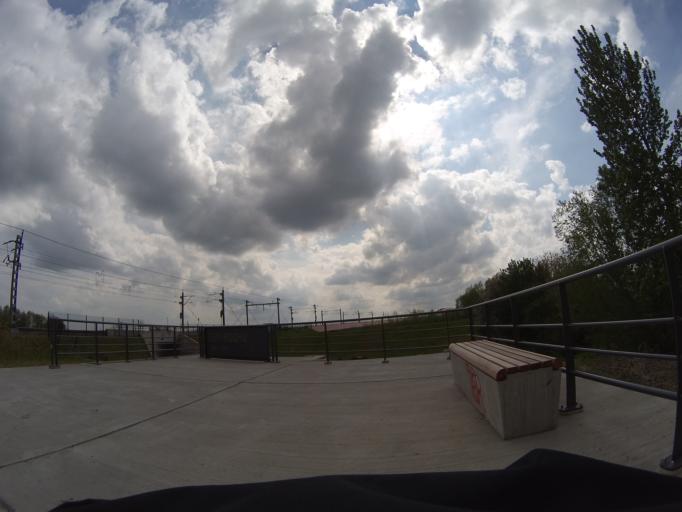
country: NL
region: Gelderland
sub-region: Gemeente Hattem
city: Hattem
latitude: 52.4932
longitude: 6.0705
